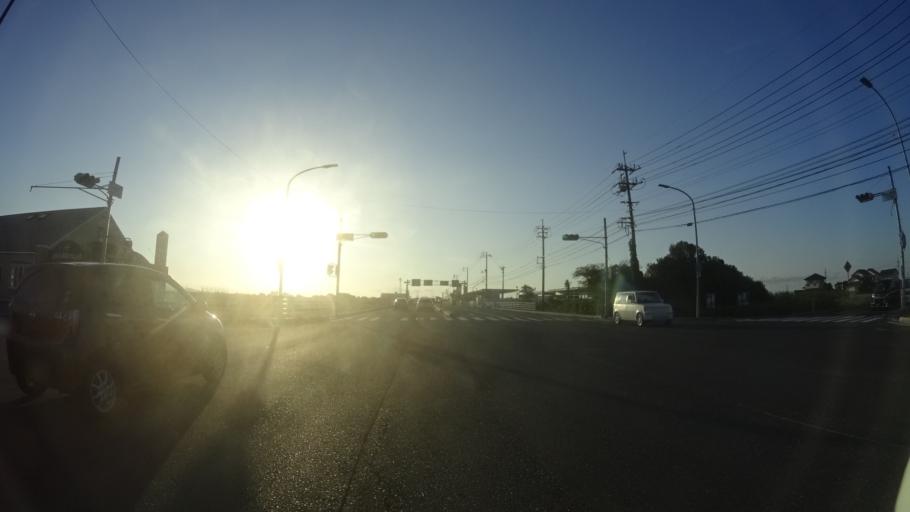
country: JP
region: Tottori
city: Yonago
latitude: 35.4461
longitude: 133.3796
